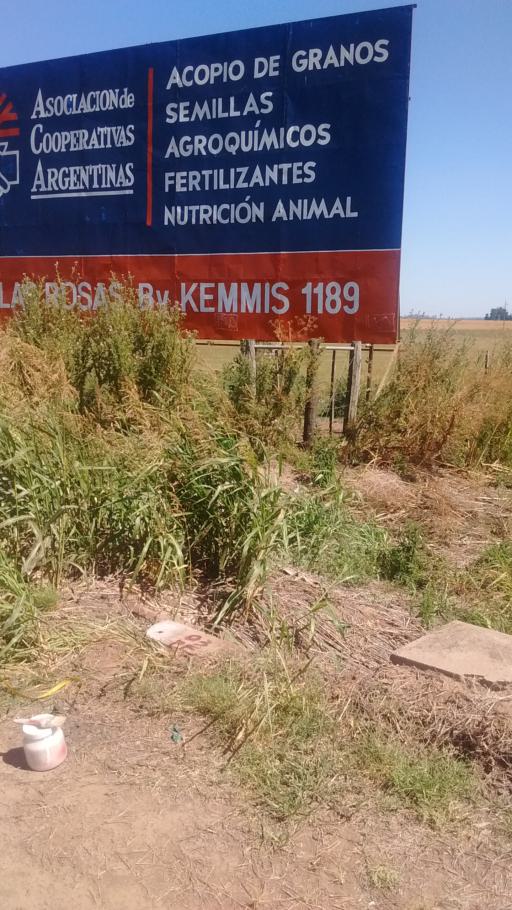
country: AR
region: Santa Fe
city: Las Rosas
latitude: -32.5357
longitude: -61.5511
